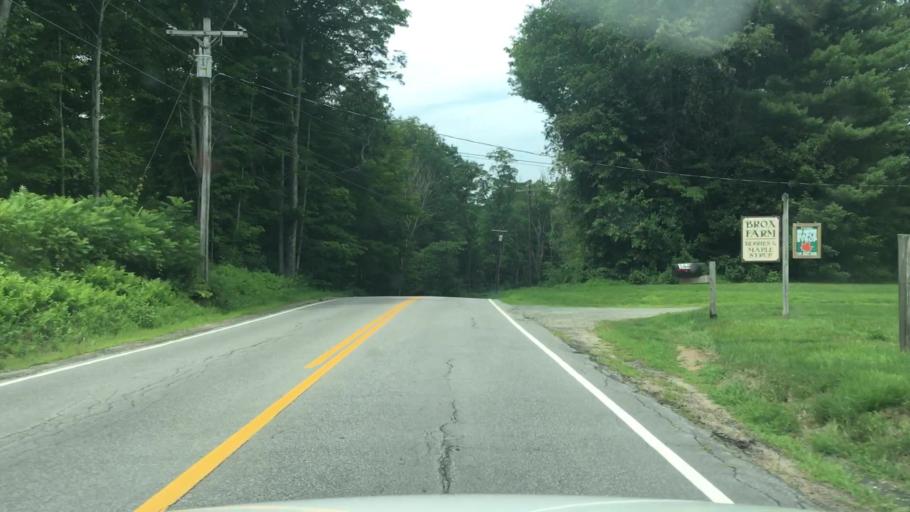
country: US
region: New Hampshire
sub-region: Grafton County
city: Rumney
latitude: 43.7839
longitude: -71.7683
